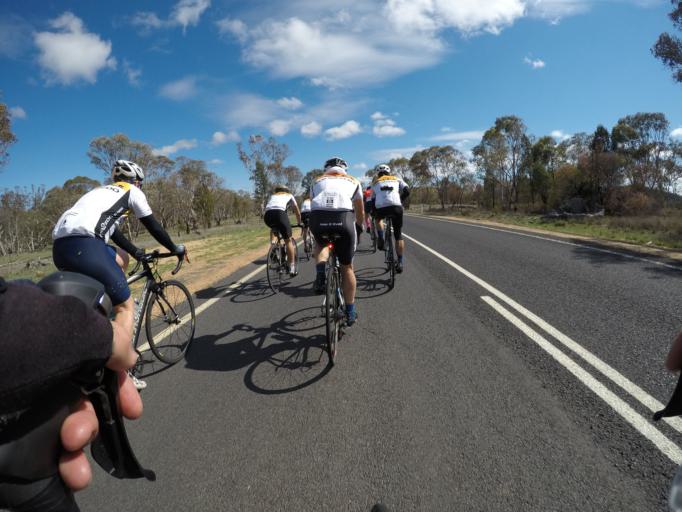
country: AU
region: New South Wales
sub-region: Parkes
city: Peak Hill
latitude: -32.6927
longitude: 148.5557
